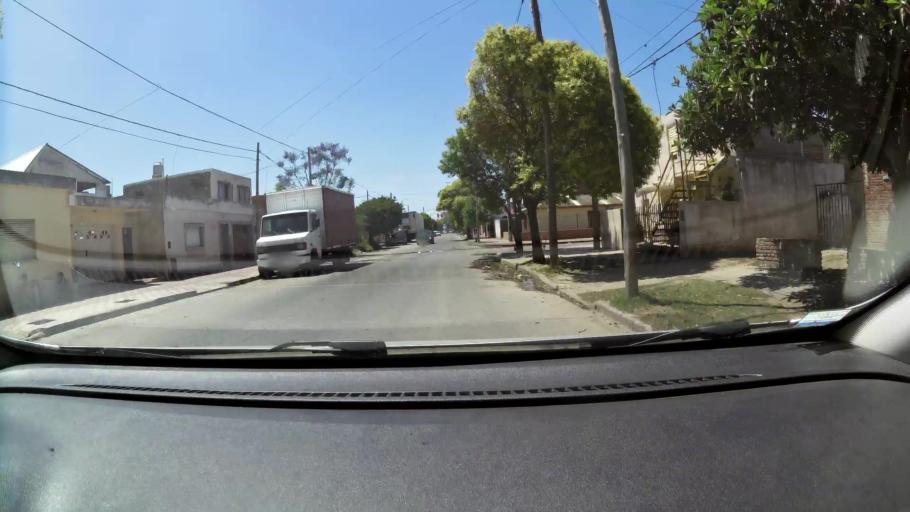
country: AR
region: Cordoba
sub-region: Departamento de Capital
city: Cordoba
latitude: -31.3835
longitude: -64.1479
